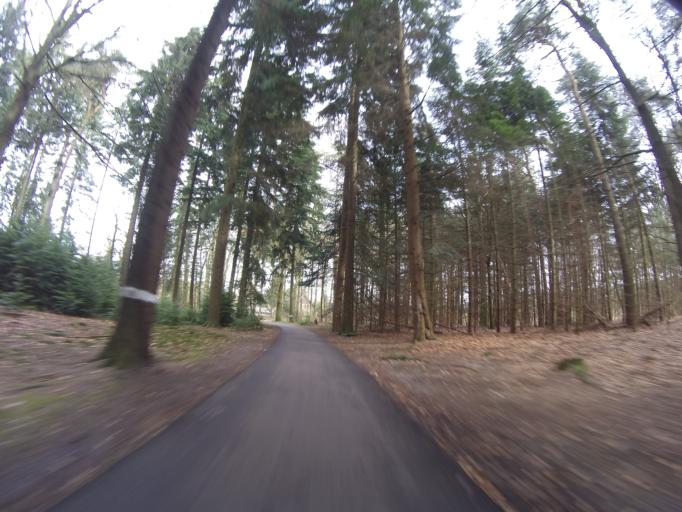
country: NL
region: Utrecht
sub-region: Gemeente Utrechtse Heuvelrug
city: Driebergen-Rijsenburg
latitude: 52.0648
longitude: 5.2717
